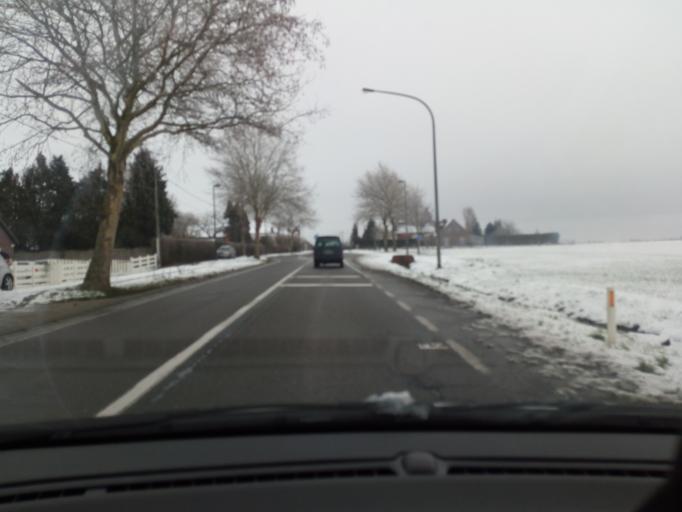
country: BE
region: Wallonia
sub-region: Province du Hainaut
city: Binche
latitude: 50.4107
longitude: 4.1353
